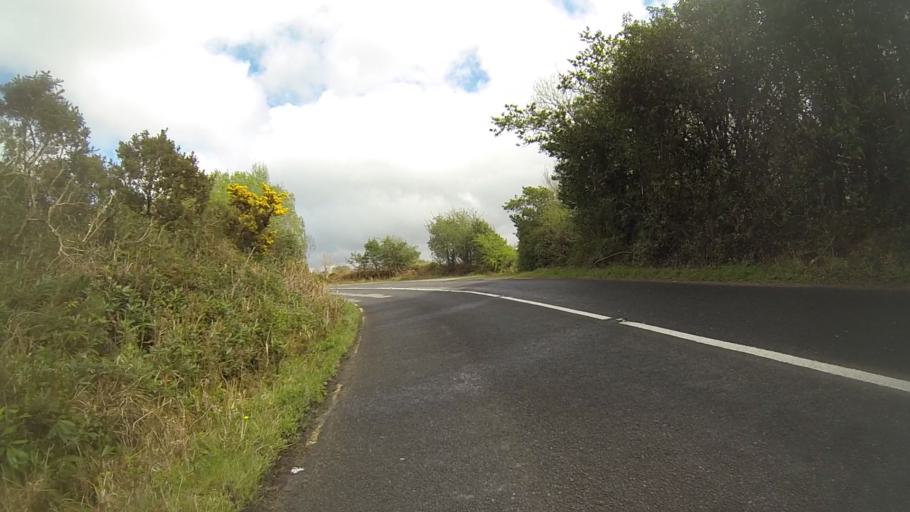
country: IE
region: Munster
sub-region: Ciarrai
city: Kenmare
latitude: 51.8264
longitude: -9.8427
